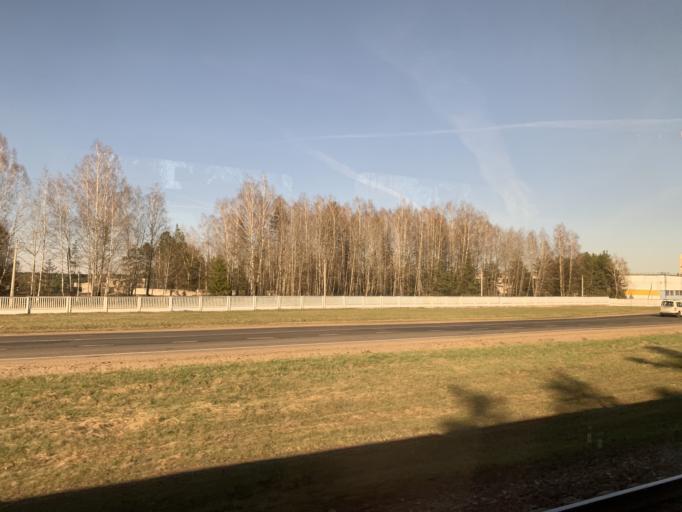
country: BY
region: Grodnenskaya
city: Smarhon'
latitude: 54.4397
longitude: 26.5062
